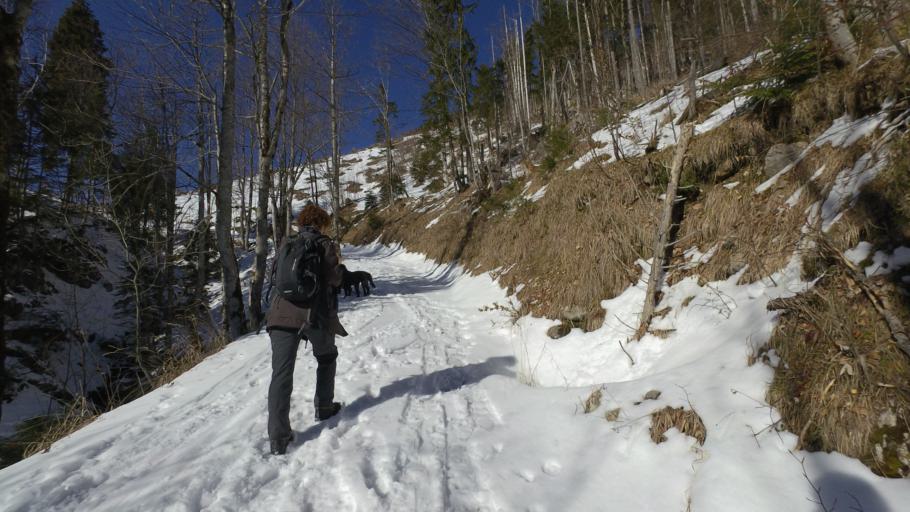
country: DE
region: Bavaria
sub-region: Upper Bavaria
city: Bergen
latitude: 47.7547
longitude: 12.5861
